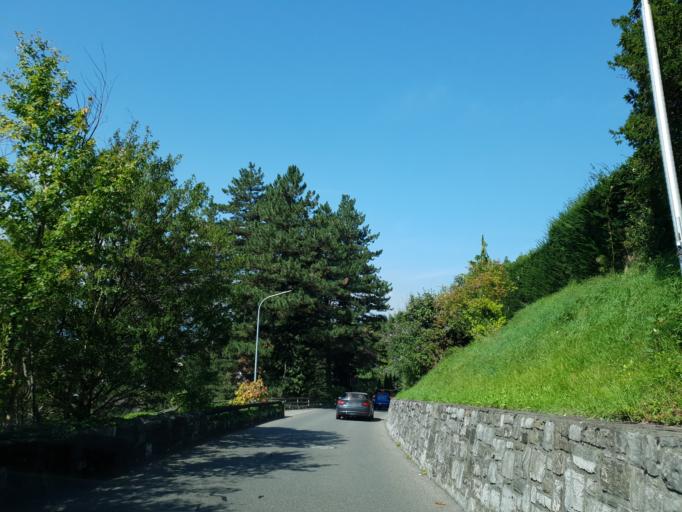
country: LI
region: Vaduz
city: Vaduz
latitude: 47.1438
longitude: 9.5236
